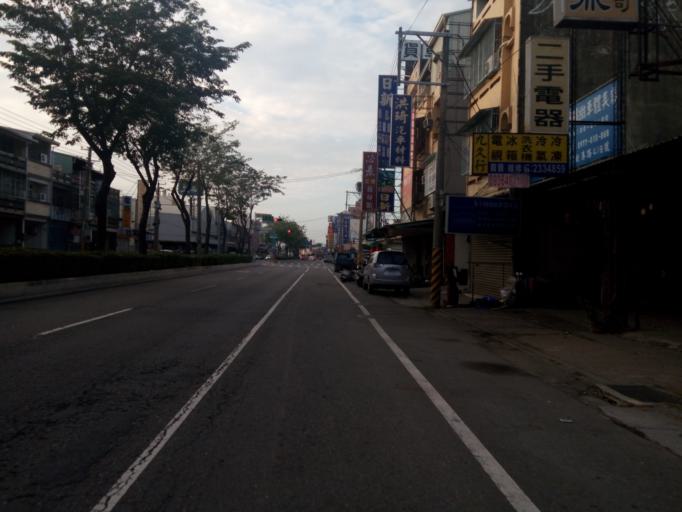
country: TW
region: Taiwan
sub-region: Chiayi
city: Jiayi Shi
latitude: 23.4830
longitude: 120.4254
